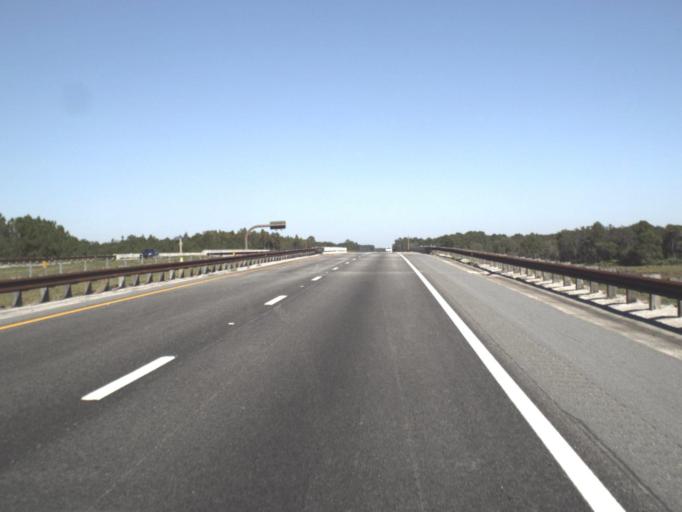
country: US
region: Florida
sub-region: Pasco County
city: Odessa
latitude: 28.2809
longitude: -82.5502
